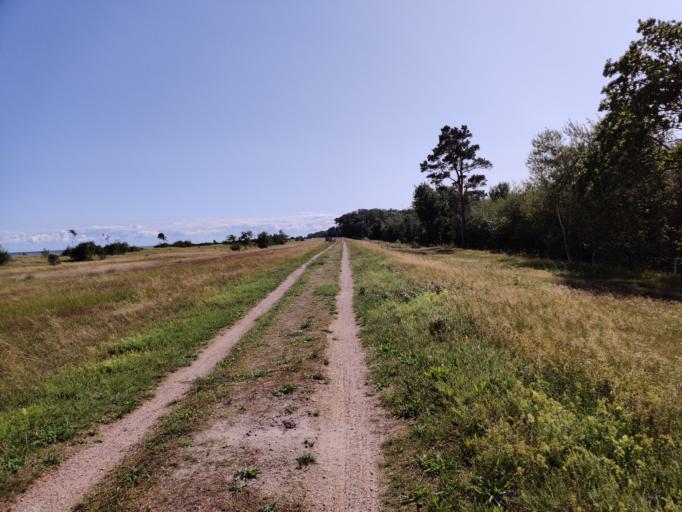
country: DK
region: Zealand
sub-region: Guldborgsund Kommune
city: Nykobing Falster
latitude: 54.6259
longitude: 11.9622
